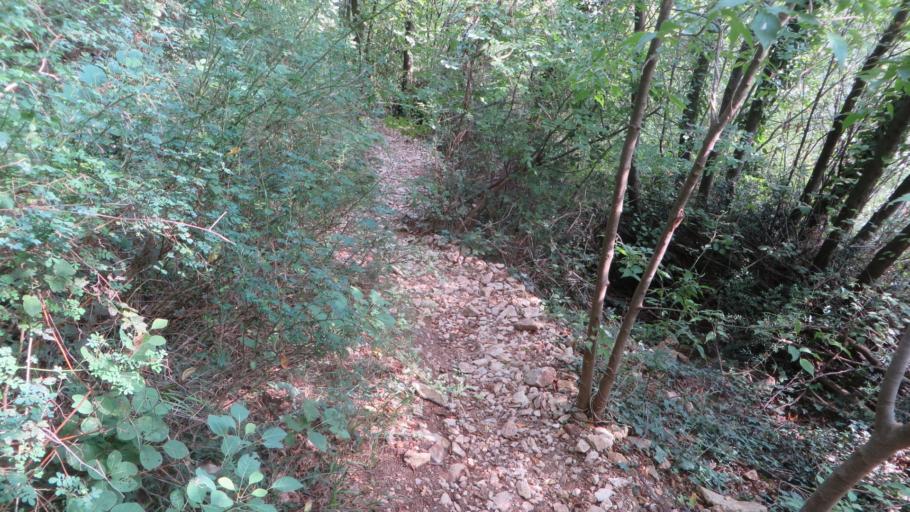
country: IT
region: Lombardy
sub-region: Provincia di Brescia
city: Solarolo
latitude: 45.5519
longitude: 10.5772
